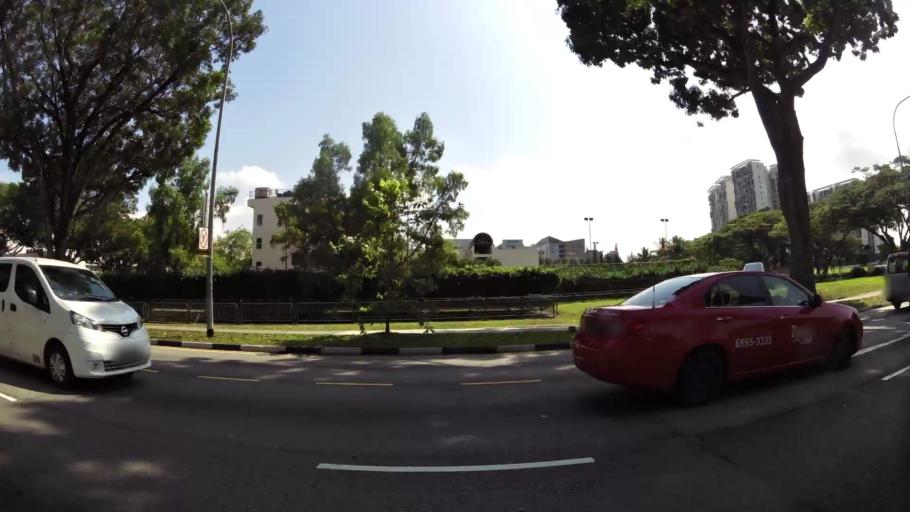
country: SG
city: Singapore
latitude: 1.3779
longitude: 103.8447
